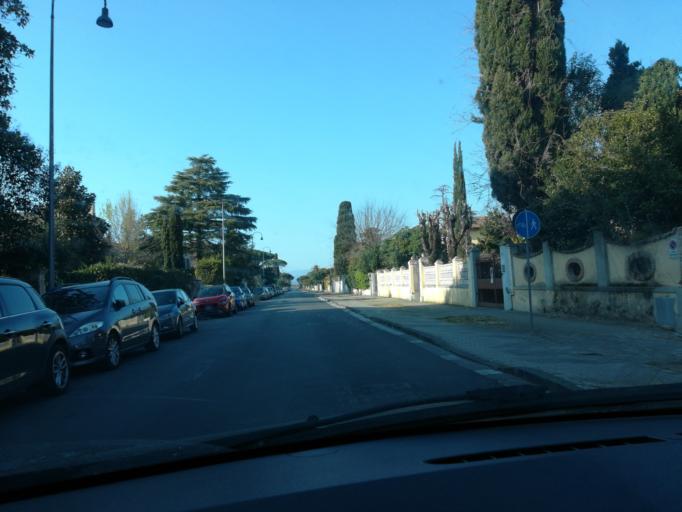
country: IT
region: Tuscany
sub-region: Province of Pisa
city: Pisa
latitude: 43.7275
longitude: 10.4027
